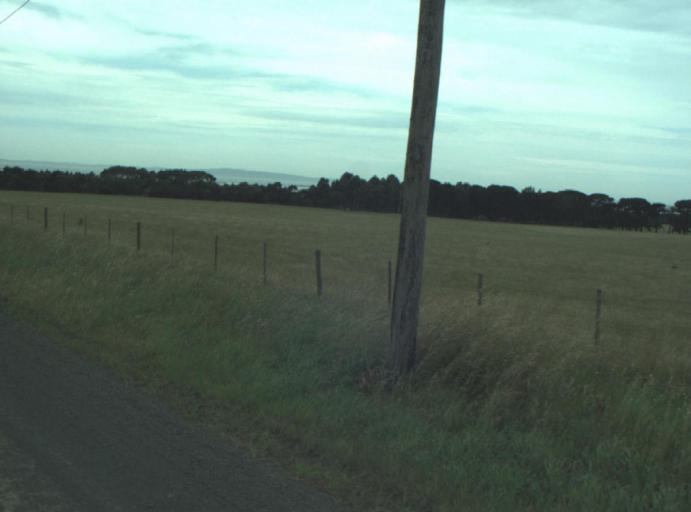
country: AU
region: Victoria
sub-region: Greater Geelong
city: Clifton Springs
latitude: -38.1924
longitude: 144.6089
